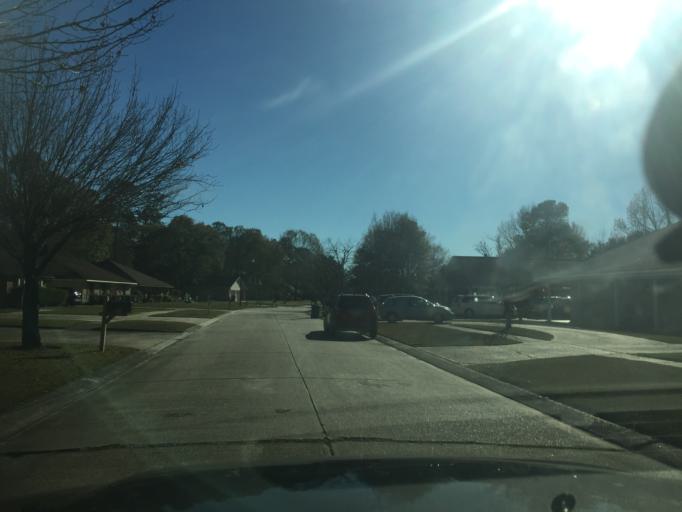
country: US
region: Louisiana
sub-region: Saint Tammany Parish
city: Slidell
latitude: 30.3041
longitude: -89.7455
